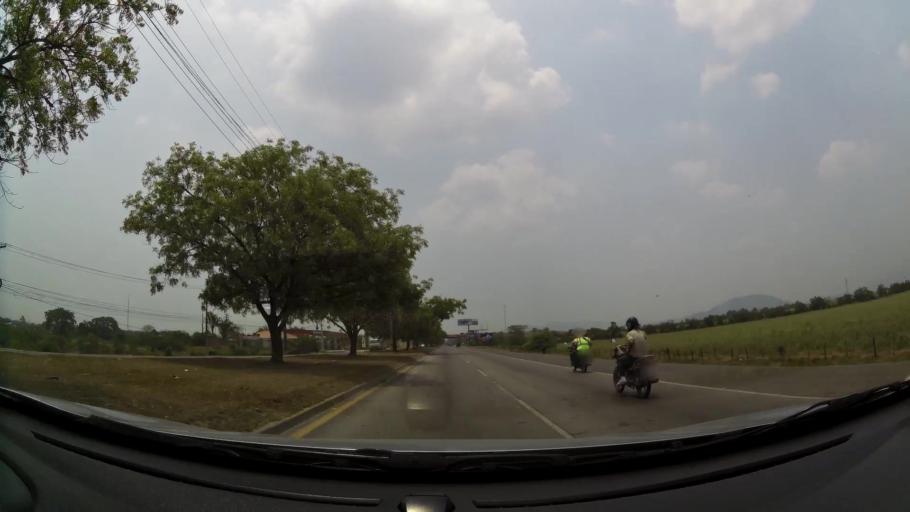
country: HN
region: Cortes
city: La Lima
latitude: 15.4479
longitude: -87.9442
